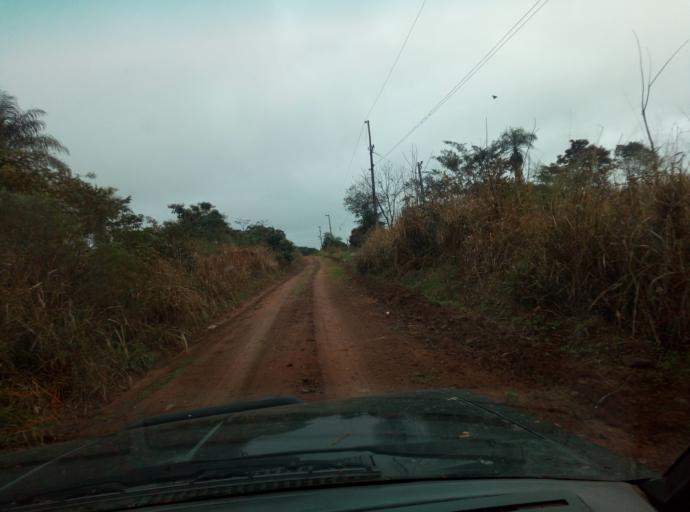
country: PY
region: Caaguazu
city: Carayao
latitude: -25.1904
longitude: -56.3554
